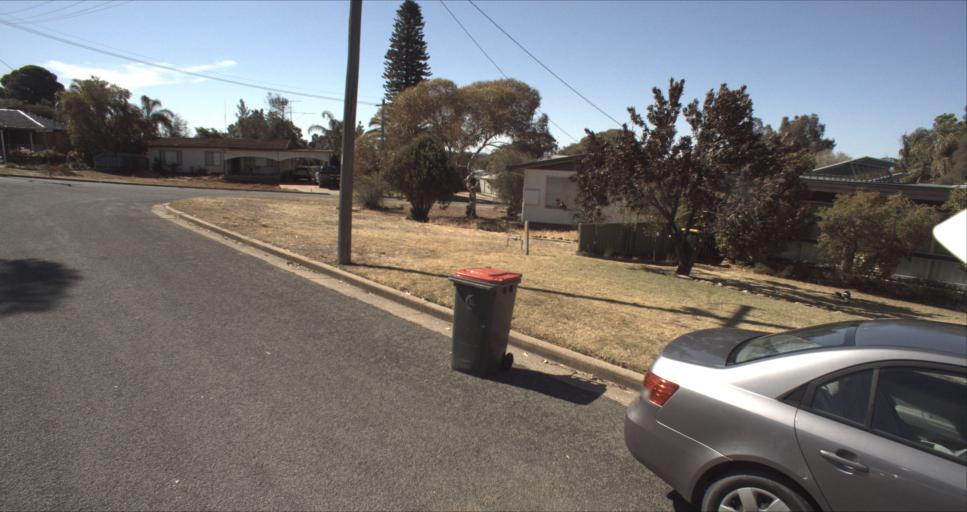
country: AU
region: New South Wales
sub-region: Leeton
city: Leeton
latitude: -34.5501
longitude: 146.3773
